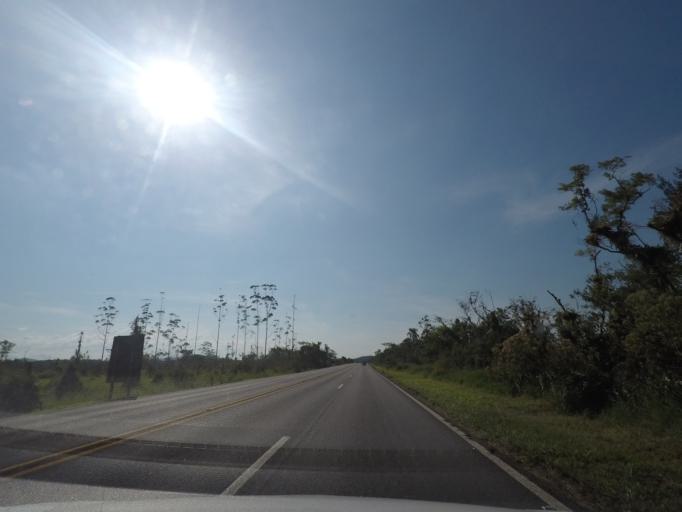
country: BR
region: Parana
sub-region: Paranagua
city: Paranagua
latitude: -25.5842
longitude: -48.6120
